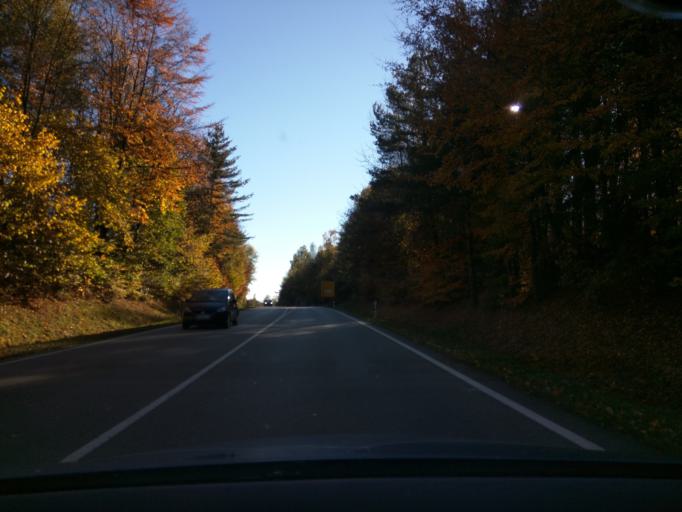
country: DE
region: Bavaria
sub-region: Lower Bavaria
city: Salzweg
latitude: 48.6007
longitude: 13.4772
